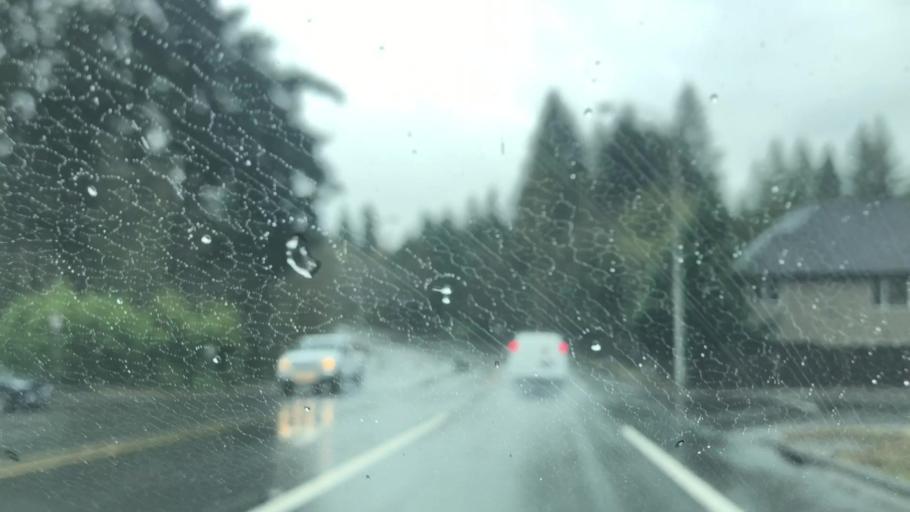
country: US
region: Oregon
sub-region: Washington County
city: Cedar Mill
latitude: 45.5230
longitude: -122.7928
